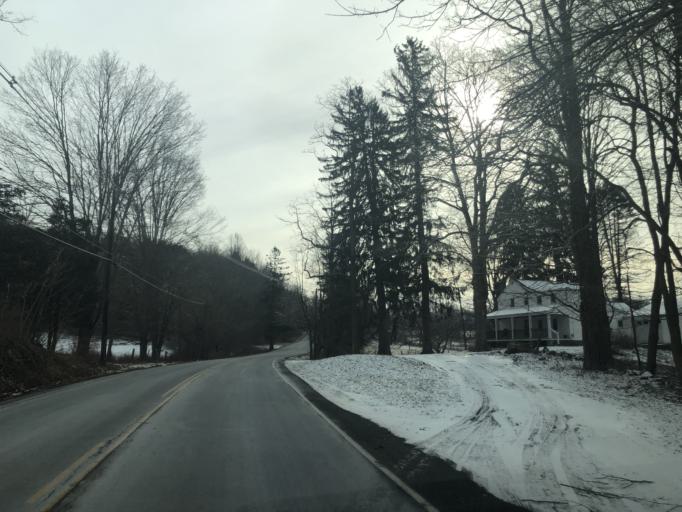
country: US
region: New Jersey
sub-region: Warren County
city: Oxford
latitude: 40.9207
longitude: -74.9885
